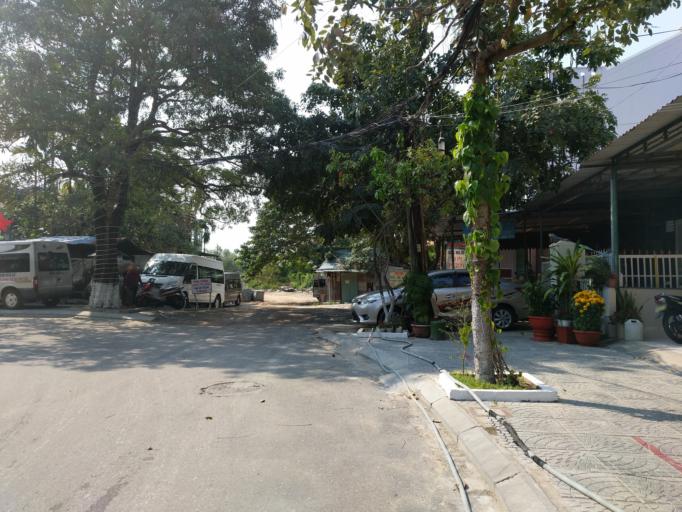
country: VN
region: Quang Nam
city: Hoi An
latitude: 15.8833
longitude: 108.3247
